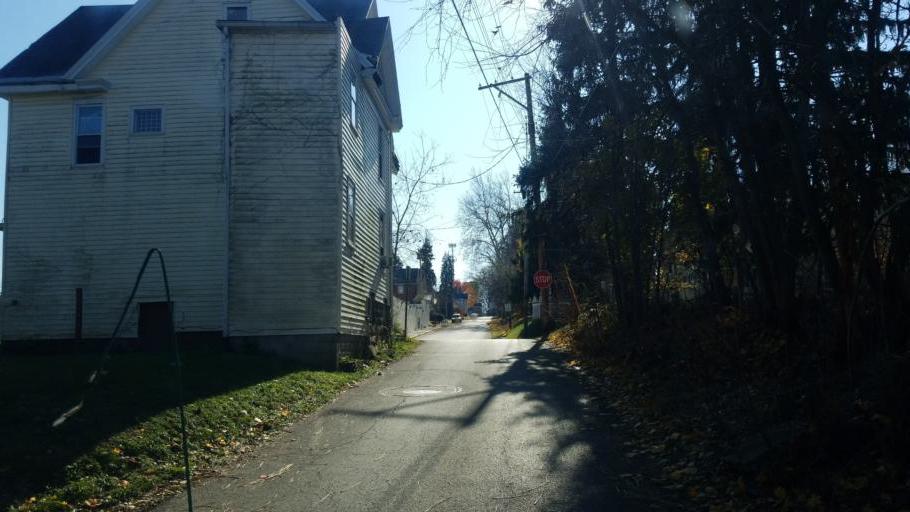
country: US
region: Ohio
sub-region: Richland County
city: Mansfield
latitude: 40.7620
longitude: -82.5288
